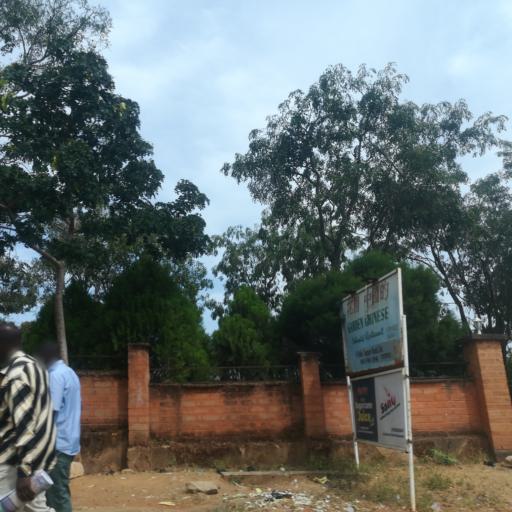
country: NG
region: Plateau
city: Jos
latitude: 9.9105
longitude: 8.8852
